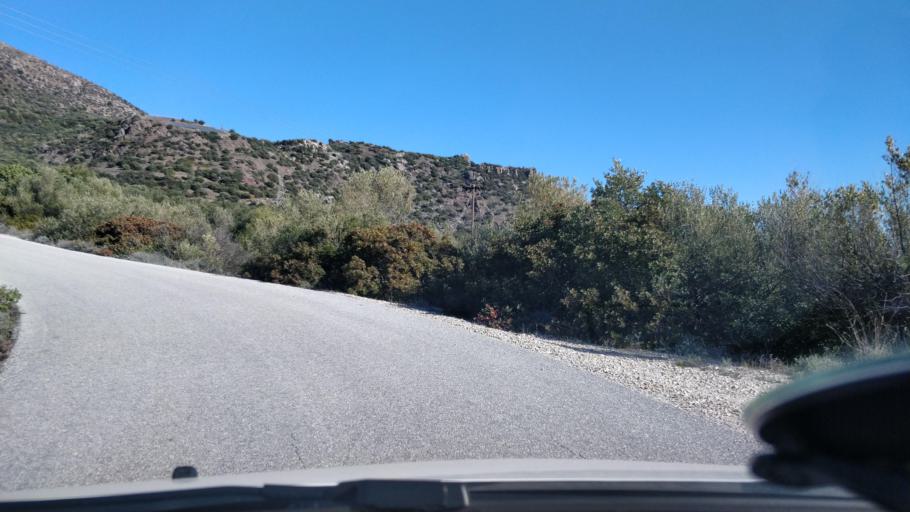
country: GR
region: Crete
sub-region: Nomos Lasithiou
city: Gra Liyia
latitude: 35.0190
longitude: 25.5512
